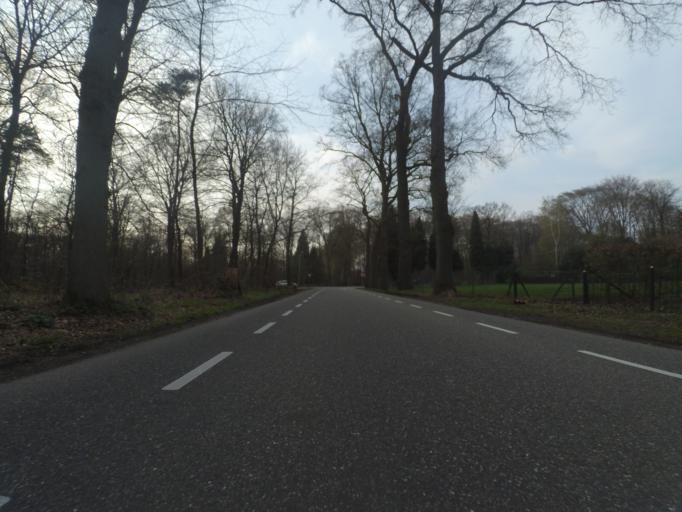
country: NL
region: Gelderland
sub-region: Gemeente Apeldoorn
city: Beekbergen
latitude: 52.1332
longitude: 5.8822
